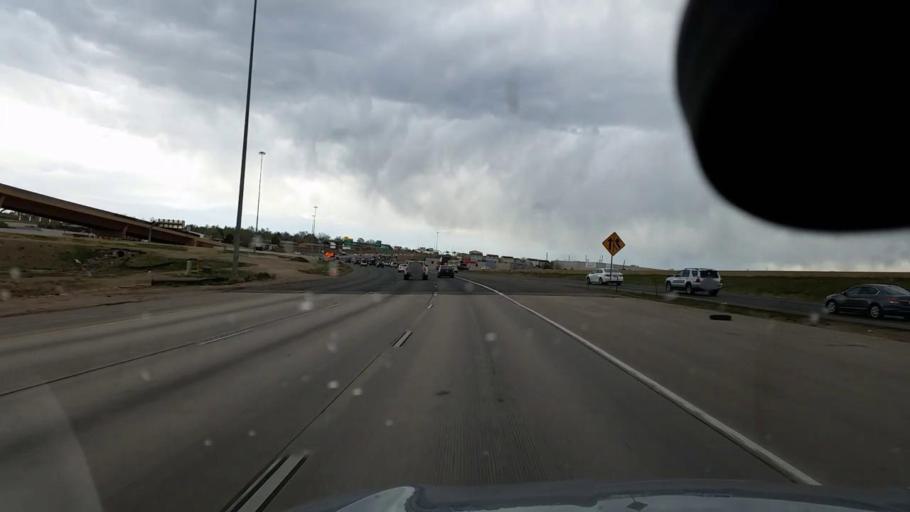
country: US
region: Colorado
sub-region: Adams County
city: Sherrelwood
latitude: 39.8285
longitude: -104.9813
